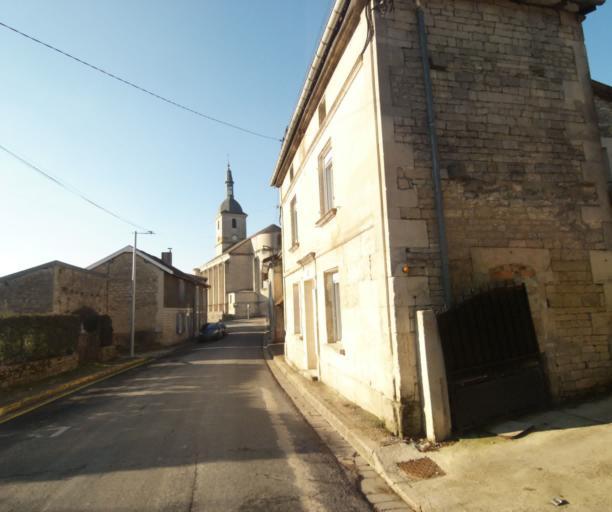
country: FR
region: Champagne-Ardenne
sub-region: Departement de la Haute-Marne
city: Chevillon
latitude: 48.5287
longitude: 5.1363
